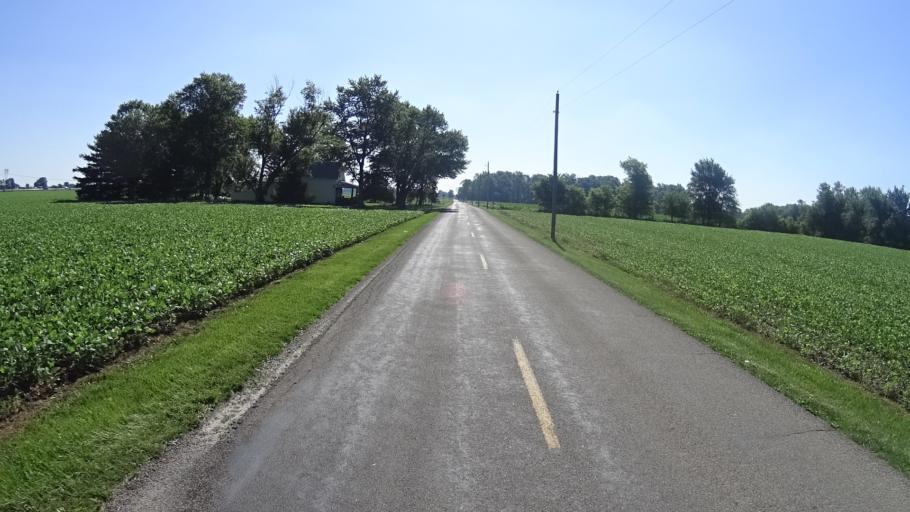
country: US
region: Indiana
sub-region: Madison County
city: Ingalls
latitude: 39.9878
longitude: -85.8271
